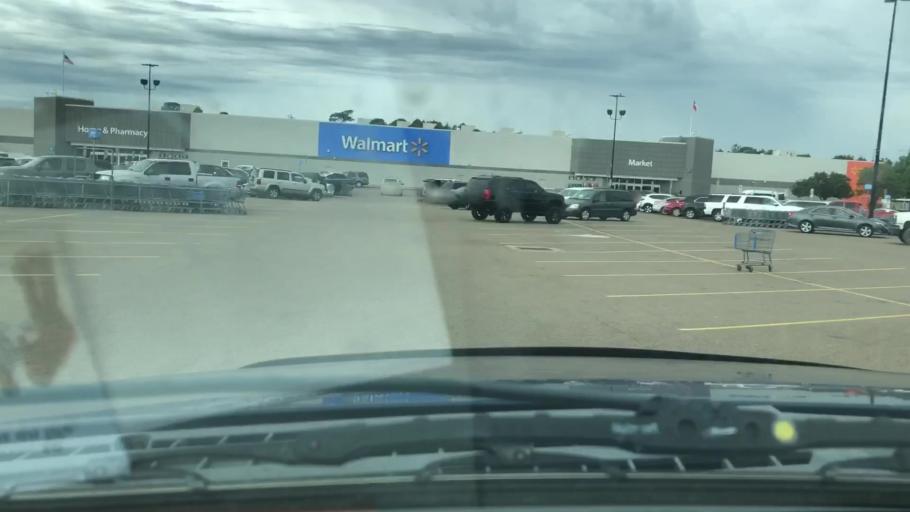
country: US
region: Texas
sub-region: Bowie County
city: Wake Village
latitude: 33.4453
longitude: -94.0994
